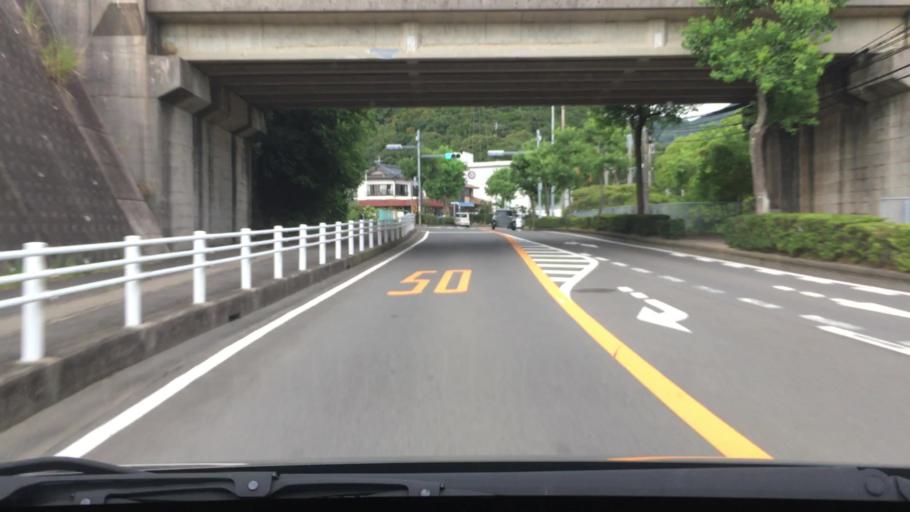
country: JP
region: Nagasaki
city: Togitsu
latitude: 32.8264
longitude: 129.7758
